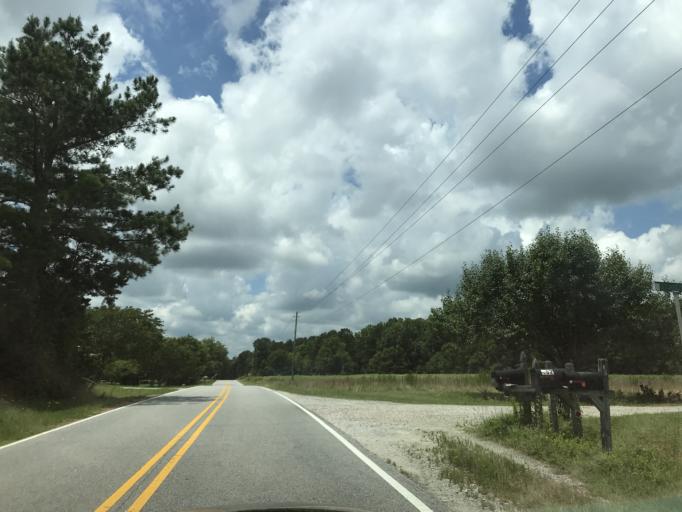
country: US
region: North Carolina
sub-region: Wake County
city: Rolesville
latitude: 35.9549
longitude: -78.3915
